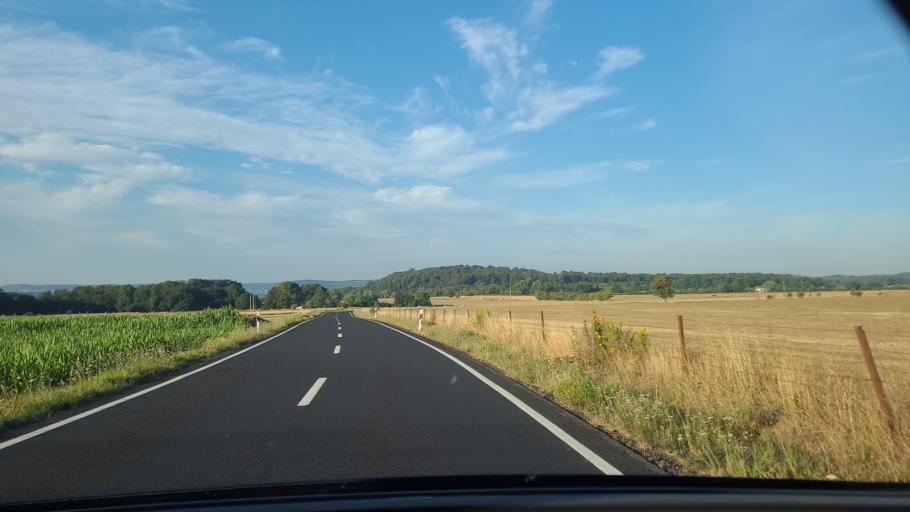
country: LU
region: Luxembourg
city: Hautcharage
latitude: 49.5996
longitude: 5.9173
